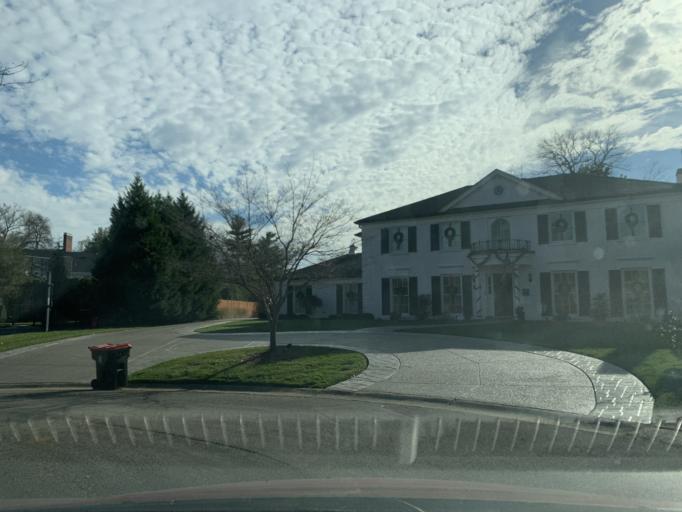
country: US
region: Kentucky
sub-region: Jefferson County
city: Saint Matthews
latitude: 38.2449
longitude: -85.6859
